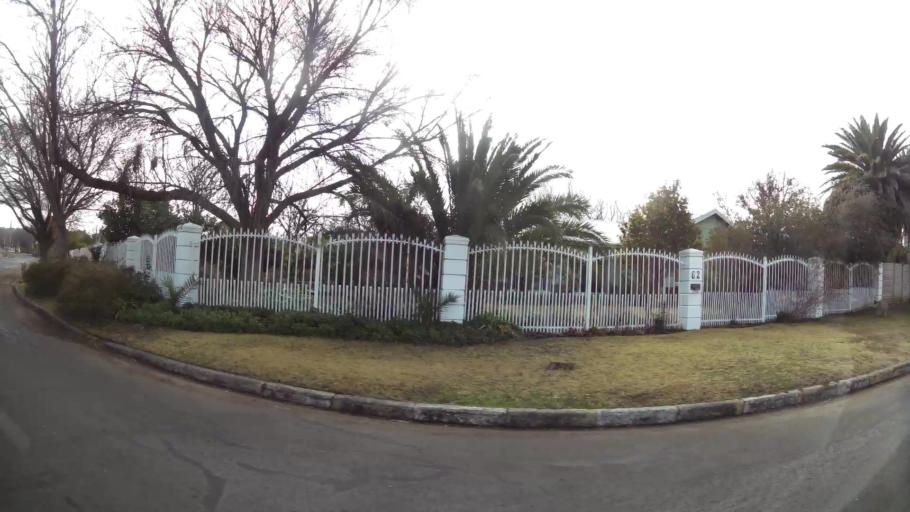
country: ZA
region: Orange Free State
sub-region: Mangaung Metropolitan Municipality
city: Bloemfontein
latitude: -29.0799
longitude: 26.2444
